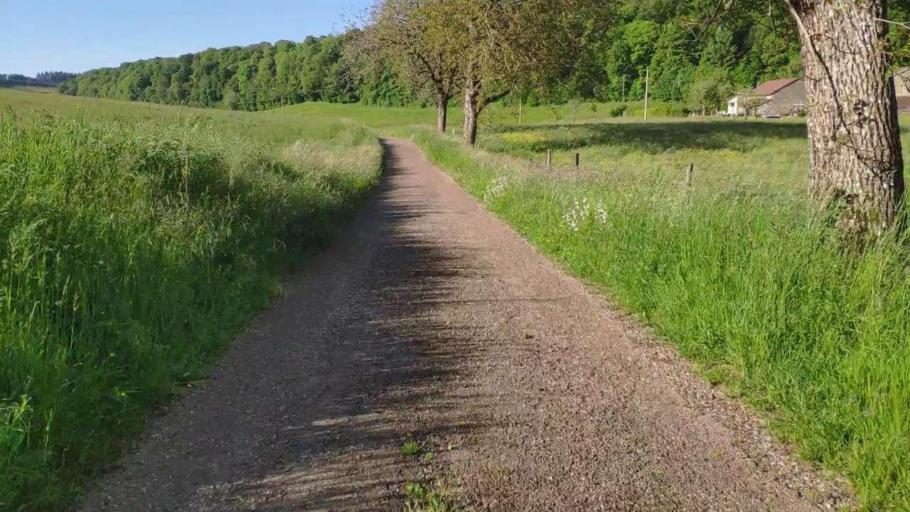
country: FR
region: Franche-Comte
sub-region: Departement du Jura
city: Perrigny
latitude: 46.7195
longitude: 5.6147
